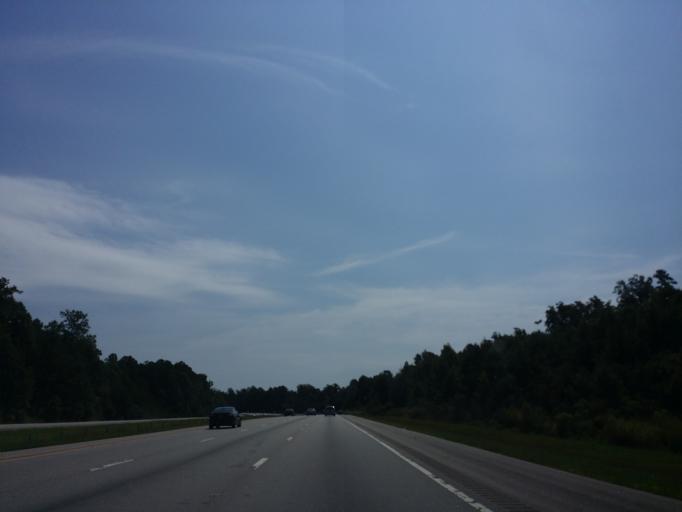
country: US
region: North Carolina
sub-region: Wake County
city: Morrisville
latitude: 35.9096
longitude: -78.7485
